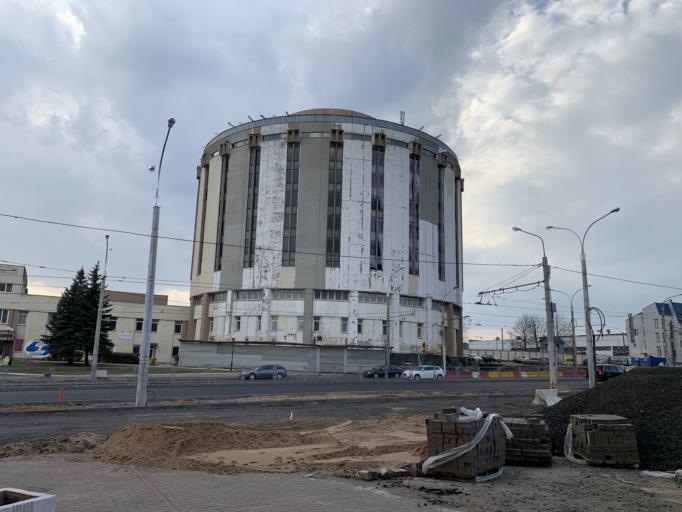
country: BY
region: Minsk
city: Minsk
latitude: 53.9000
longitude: 27.5342
